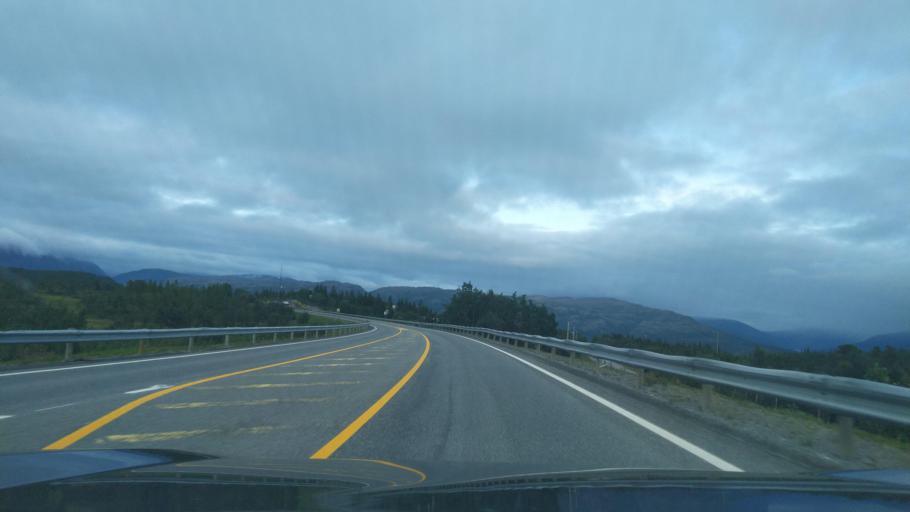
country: NO
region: Nordland
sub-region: Narvik
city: Narvik
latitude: 68.5223
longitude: 17.3814
